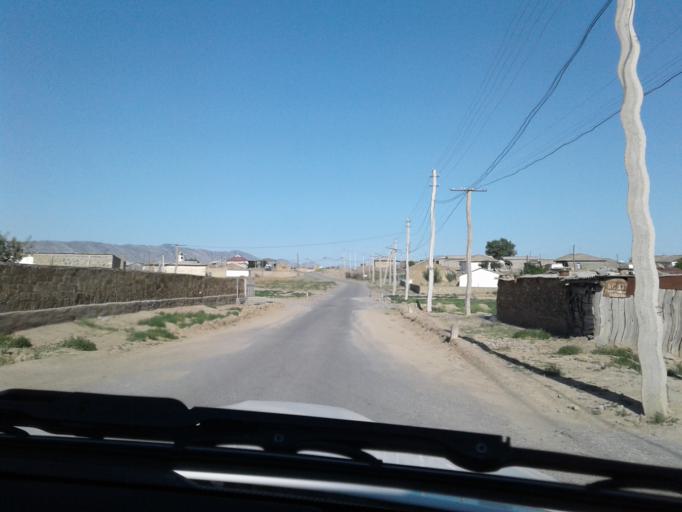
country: TM
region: Balkan
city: Magtymguly
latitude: 38.6829
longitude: 56.4577
